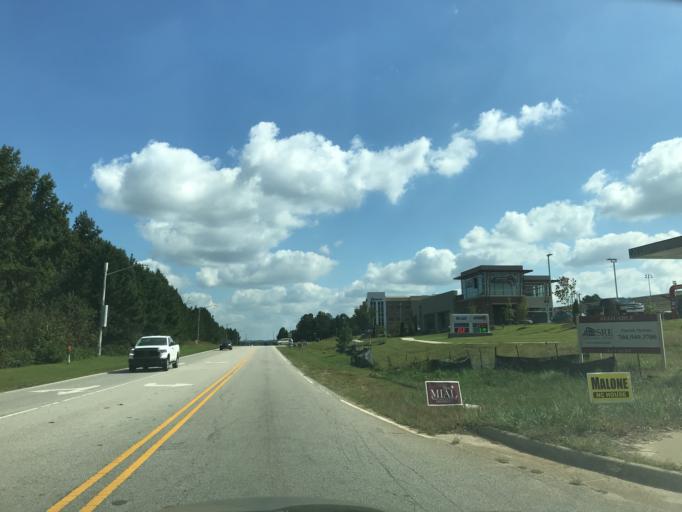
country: US
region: North Carolina
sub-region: Wake County
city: Wake Forest
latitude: 35.9525
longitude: -78.5245
